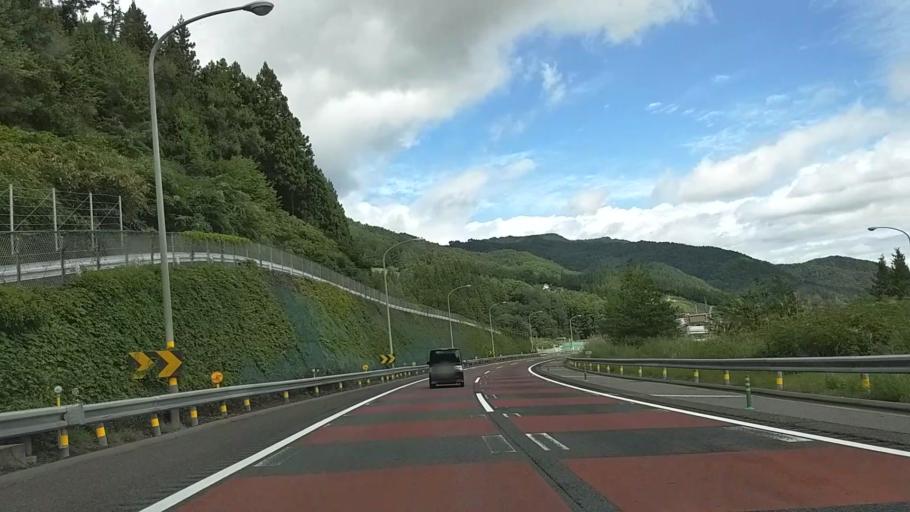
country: JP
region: Nagano
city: Nagano-shi
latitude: 36.5151
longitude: 138.0712
